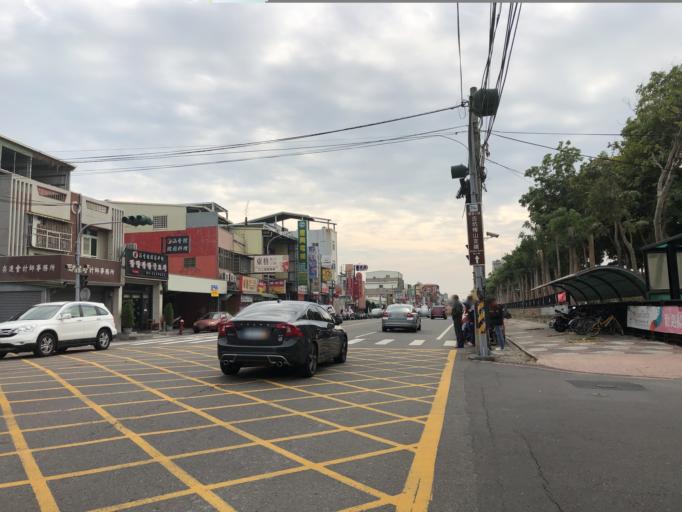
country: TW
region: Taiwan
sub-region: Yunlin
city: Douliu
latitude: 23.6943
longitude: 120.5381
